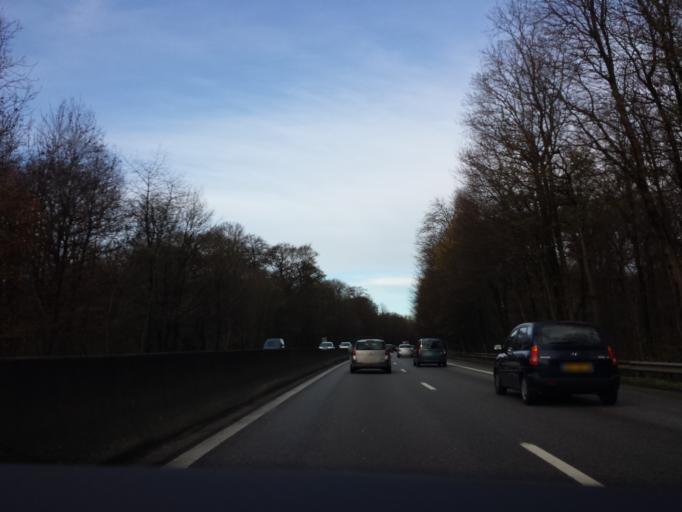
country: FR
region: Ile-de-France
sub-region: Departement des Yvelines
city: Saint-Nom-la-Breteche
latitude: 48.8674
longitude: 2.0333
